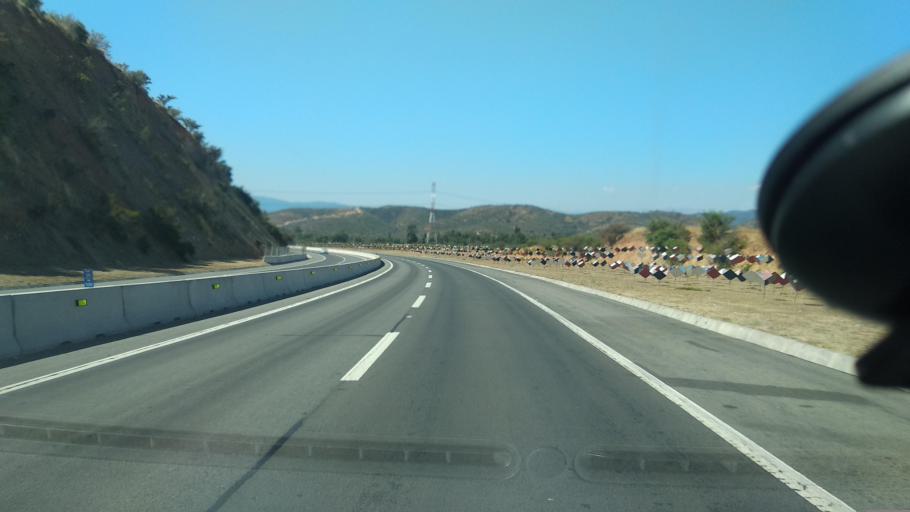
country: CL
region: Valparaiso
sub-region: Provincia de Marga Marga
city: Limache
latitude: -33.0282
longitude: -71.3190
